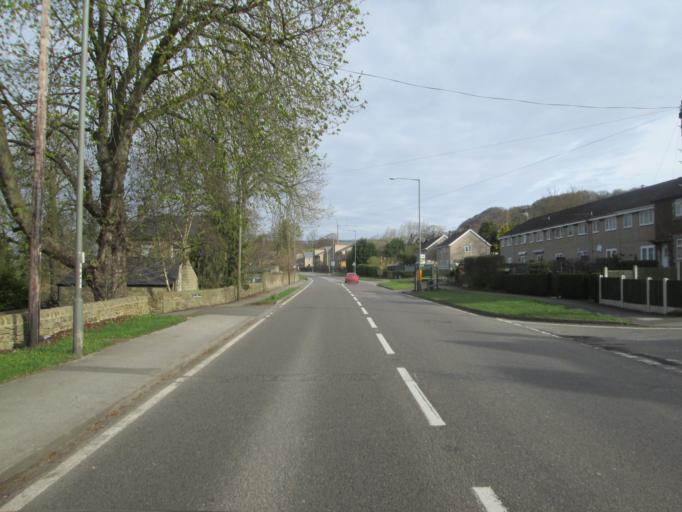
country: GB
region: England
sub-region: Derbyshire
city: Matlock
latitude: 53.1466
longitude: -1.5729
